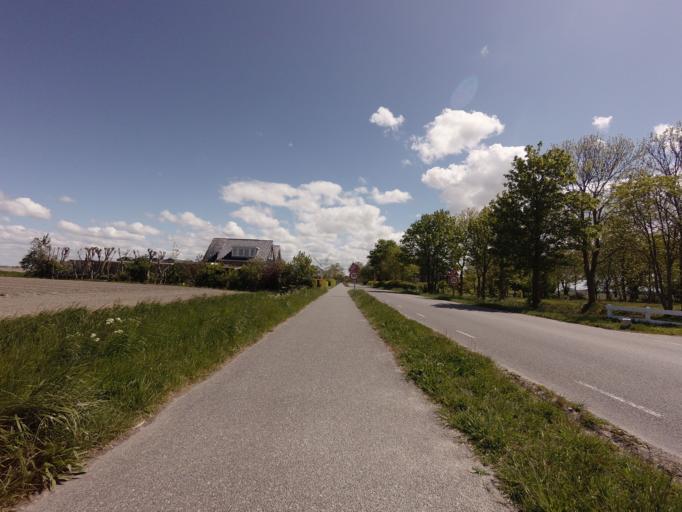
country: NL
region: Friesland
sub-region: Gemeente Harlingen
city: Harlingen
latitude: 53.1404
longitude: 5.4417
